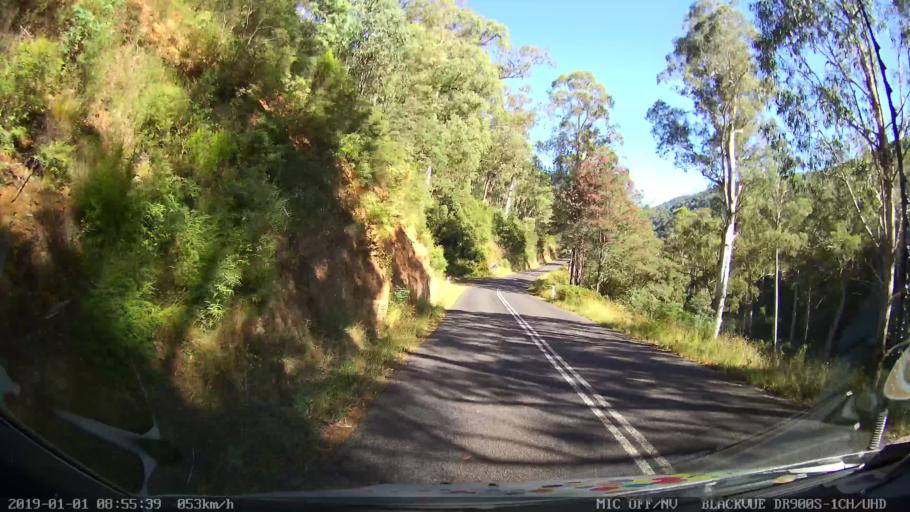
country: AU
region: New South Wales
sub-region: Snowy River
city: Jindabyne
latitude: -36.2523
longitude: 148.1911
